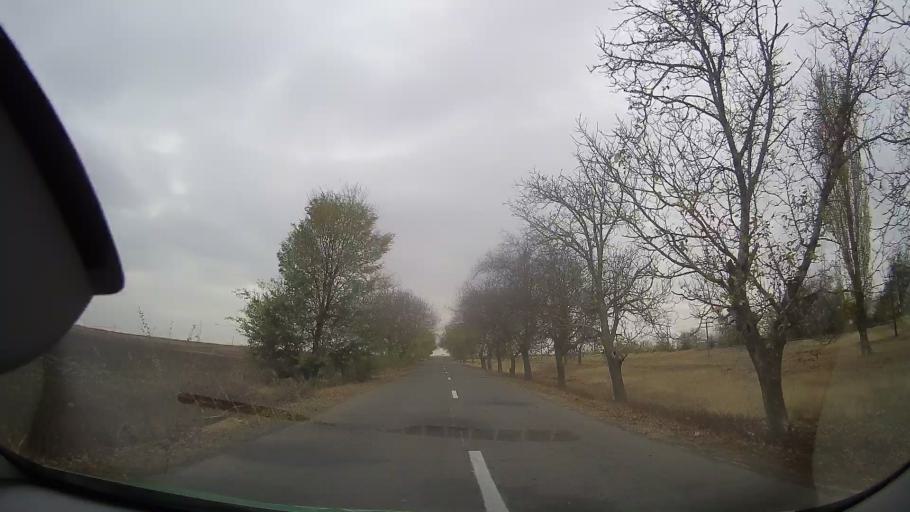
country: RO
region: Ialomita
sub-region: Comuna Garbovi
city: Garbovi
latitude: 44.7717
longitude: 26.7830
